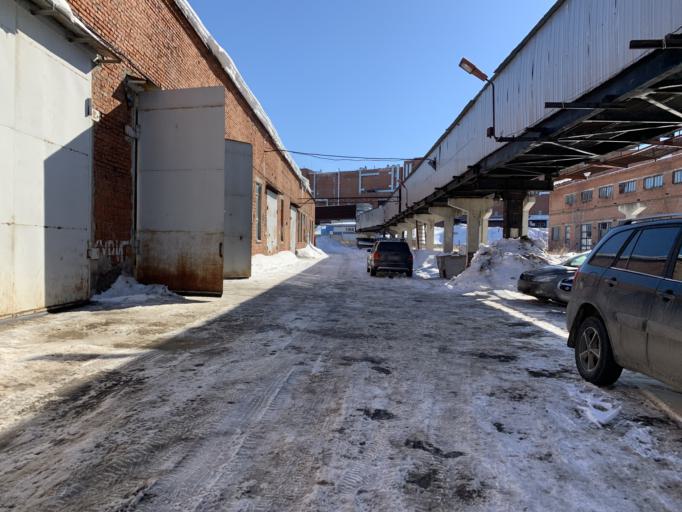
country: RU
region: Chuvashia
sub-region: Cheboksarskiy Rayon
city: Cheboksary
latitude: 56.1398
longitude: 47.2783
